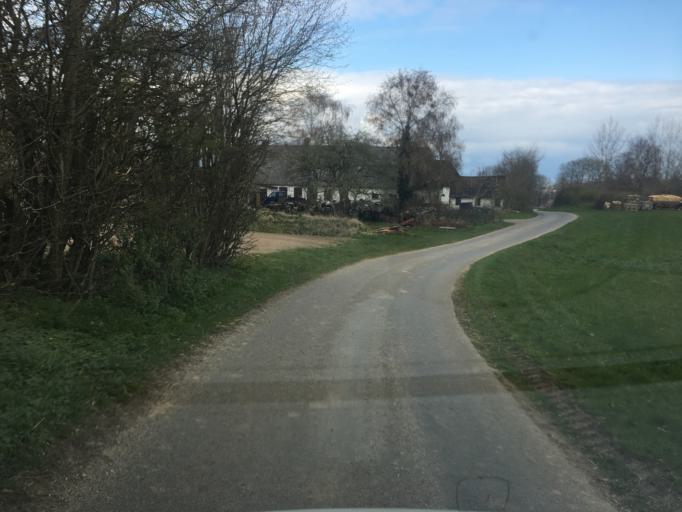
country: DK
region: South Denmark
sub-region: Aabenraa Kommune
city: Lojt Kirkeby
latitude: 55.0177
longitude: 9.5247
